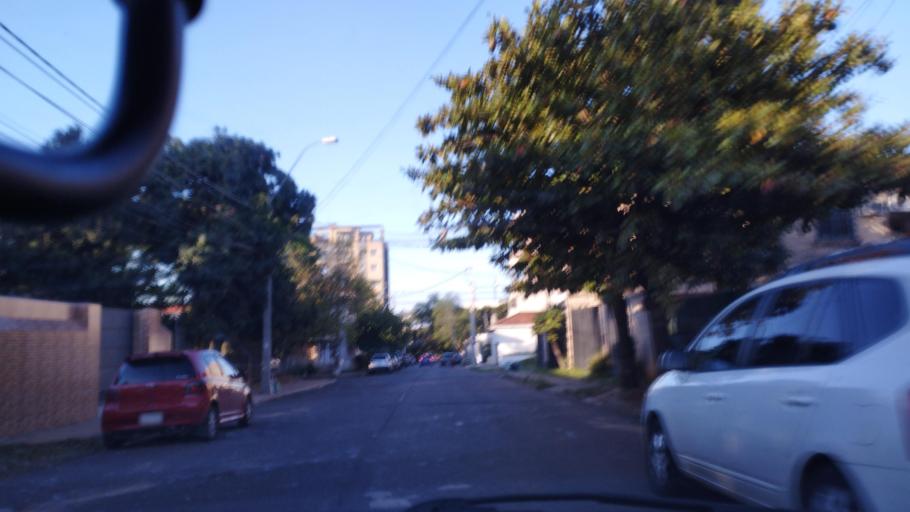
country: PY
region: Central
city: Lambare
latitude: -25.3025
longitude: -57.5850
